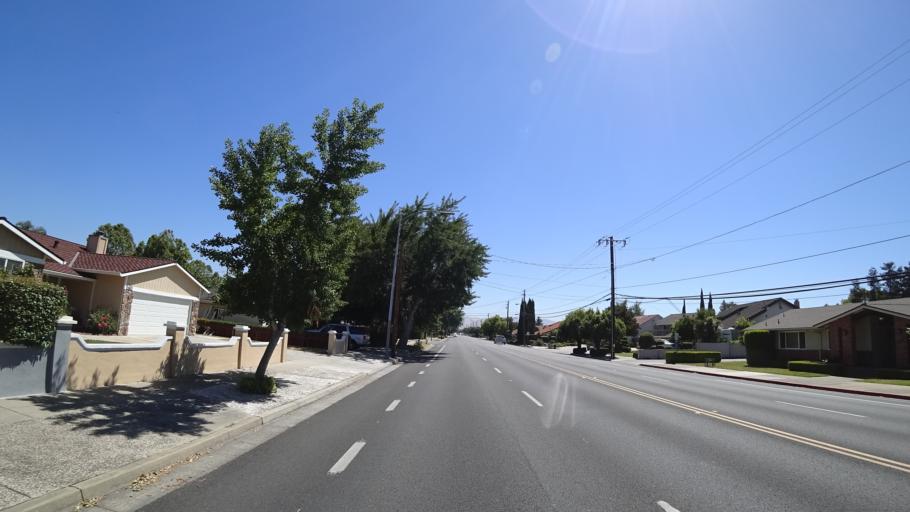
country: US
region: California
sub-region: Santa Clara County
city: Cambrian Park
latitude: 37.2845
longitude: -121.9030
